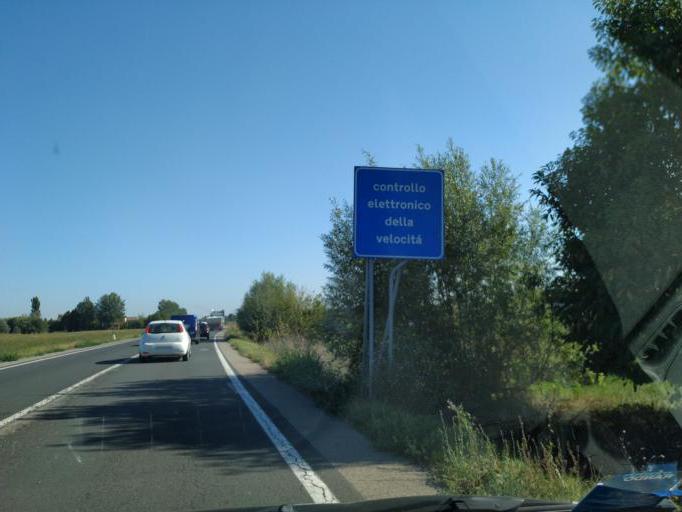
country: IT
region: Emilia-Romagna
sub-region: Provincia di Bologna
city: Decima
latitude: 44.7126
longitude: 11.2434
